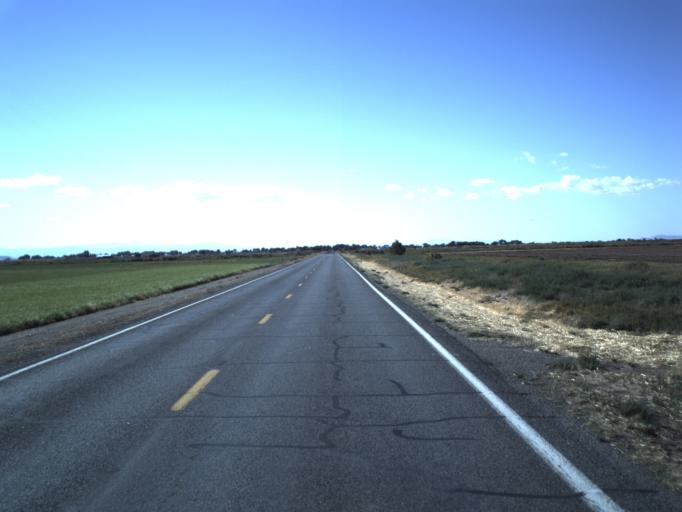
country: US
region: Utah
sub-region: Millard County
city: Delta
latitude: 39.3197
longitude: -112.6524
